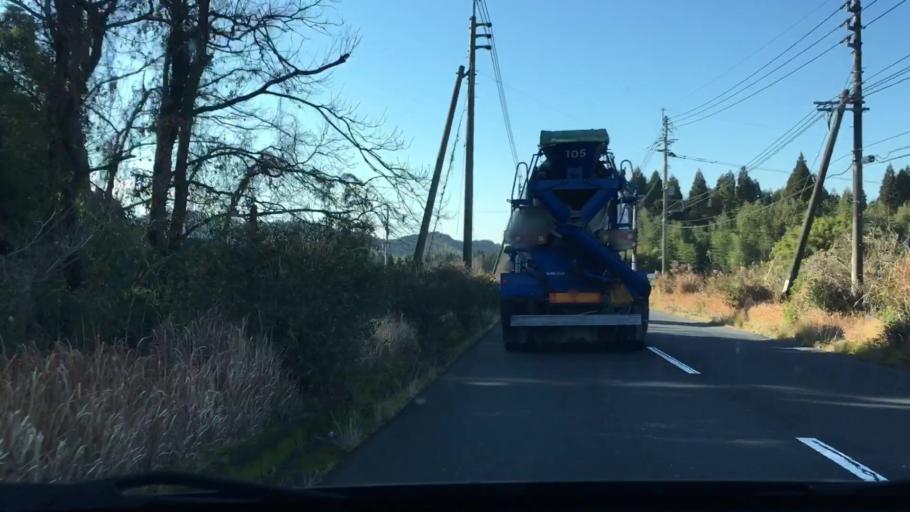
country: JP
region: Kagoshima
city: Kajiki
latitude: 31.7686
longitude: 130.6921
